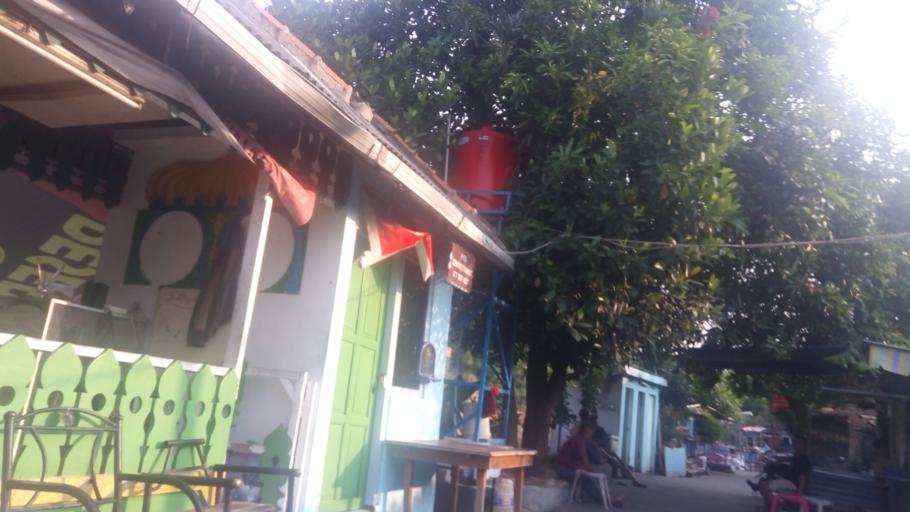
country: ID
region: Jakarta Raya
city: Jakarta
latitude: -6.2057
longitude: 106.8550
